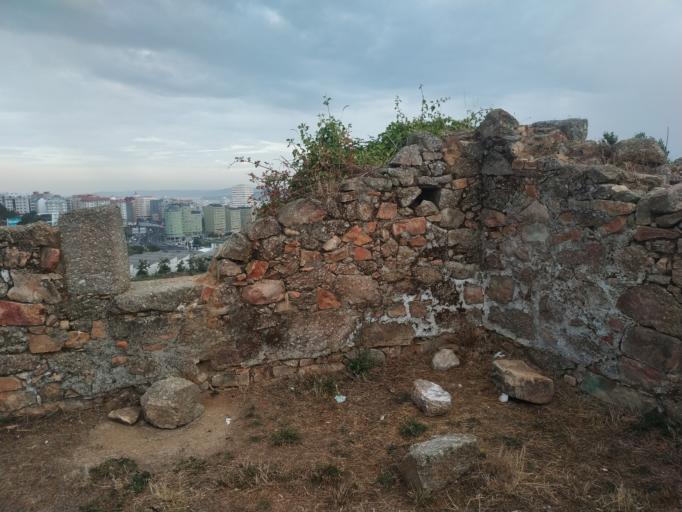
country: ES
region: Galicia
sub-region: Provincia da Coruna
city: A Coruna
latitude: 43.3460
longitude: -8.3937
